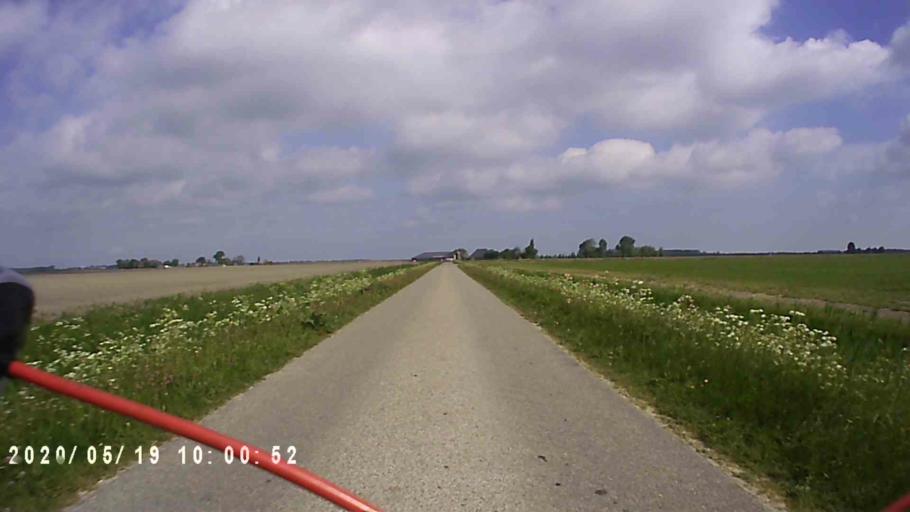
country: NL
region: Groningen
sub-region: Gemeente Zuidhorn
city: Grijpskerk
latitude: 53.3001
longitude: 6.2365
